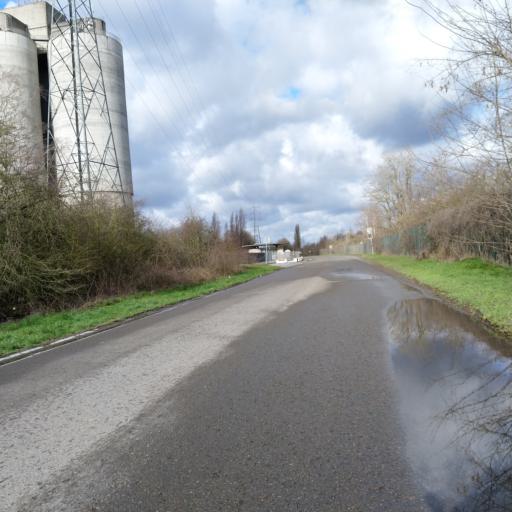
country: BE
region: Wallonia
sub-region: Province du Hainaut
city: Mons
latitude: 50.4762
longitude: 3.9979
